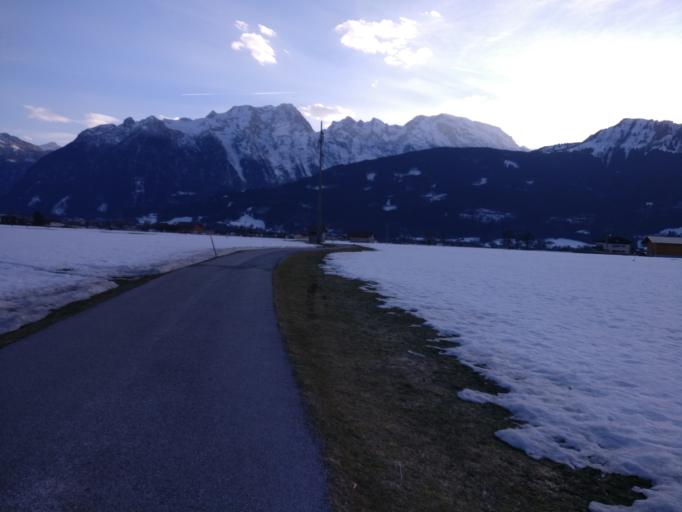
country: AT
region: Salzburg
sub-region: Politischer Bezirk Hallein
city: Kuchl
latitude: 47.6458
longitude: 13.1548
